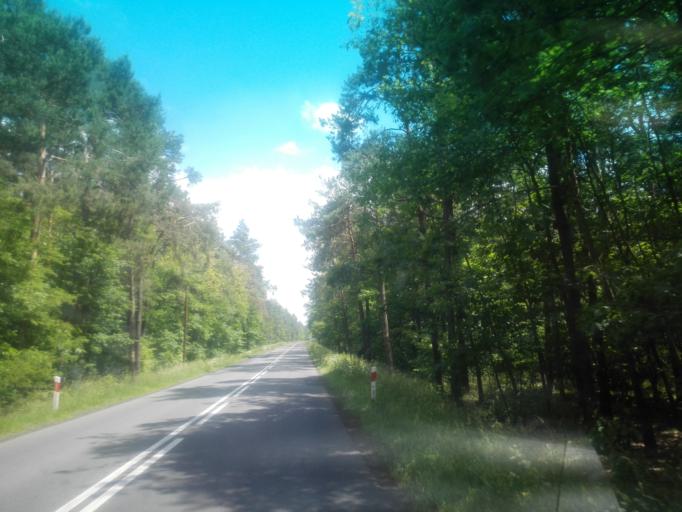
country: PL
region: Silesian Voivodeship
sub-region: Powiat czestochowski
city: Potok Zloty
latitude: 50.7399
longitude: 19.3552
